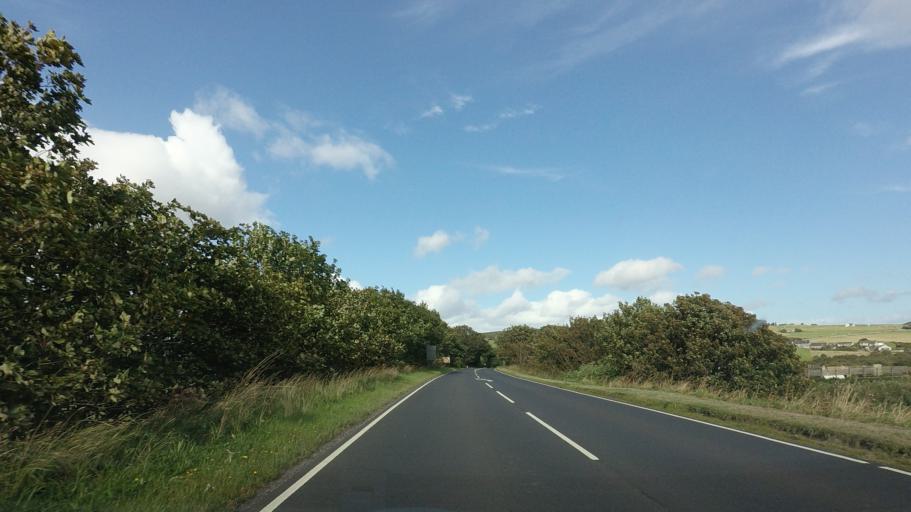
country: GB
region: Scotland
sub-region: Highland
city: Wick
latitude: 58.2718
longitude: -3.3927
